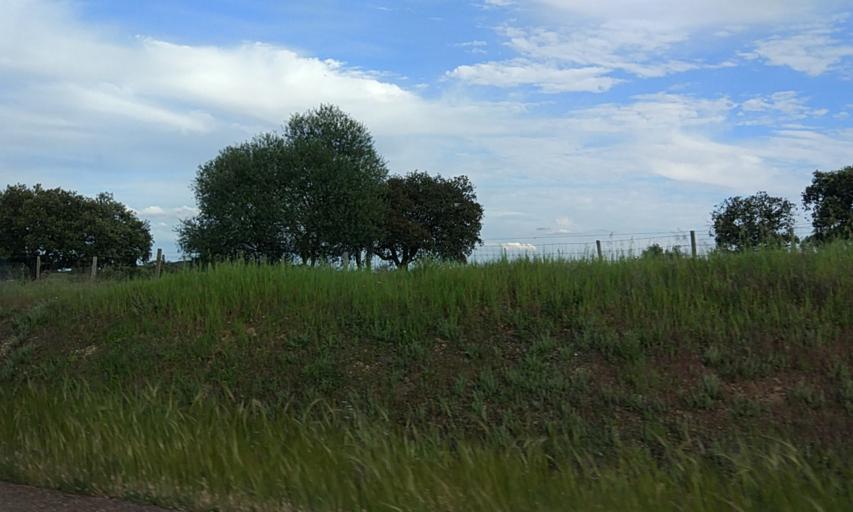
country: PT
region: Portalegre
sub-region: Elvas
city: Elvas
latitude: 38.8991
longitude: -7.2019
